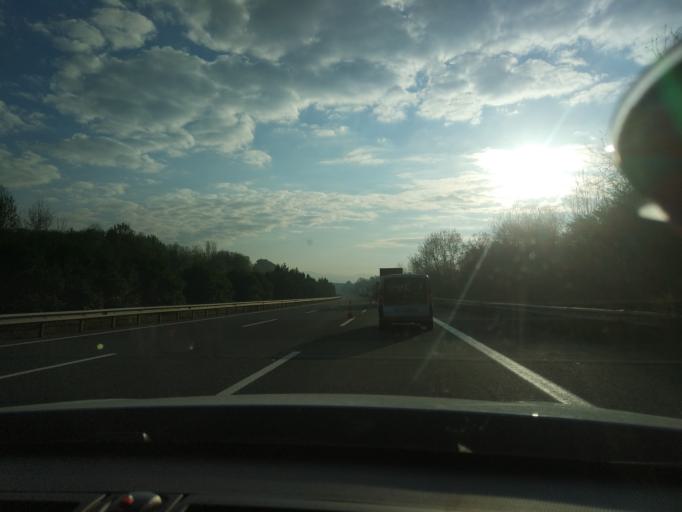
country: TR
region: Duzce
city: Duzce
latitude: 40.8106
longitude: 31.1241
